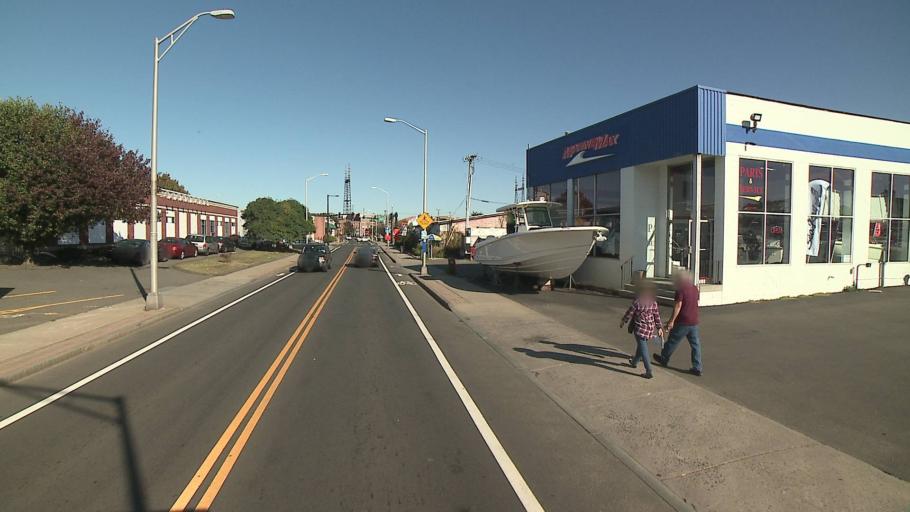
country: US
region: Connecticut
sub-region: Fairfield County
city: East Norwalk
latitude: 41.0955
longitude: -73.4156
